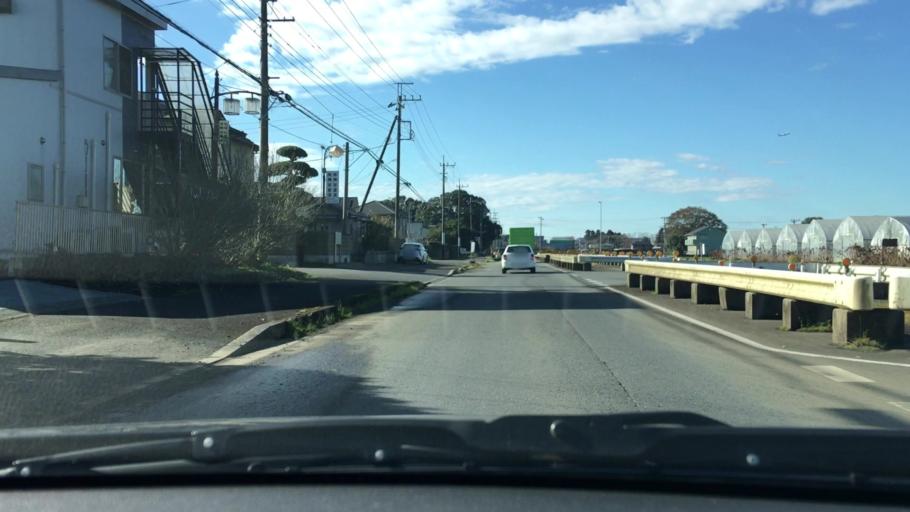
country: JP
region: Chiba
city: Narita
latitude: 35.7895
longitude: 140.4092
